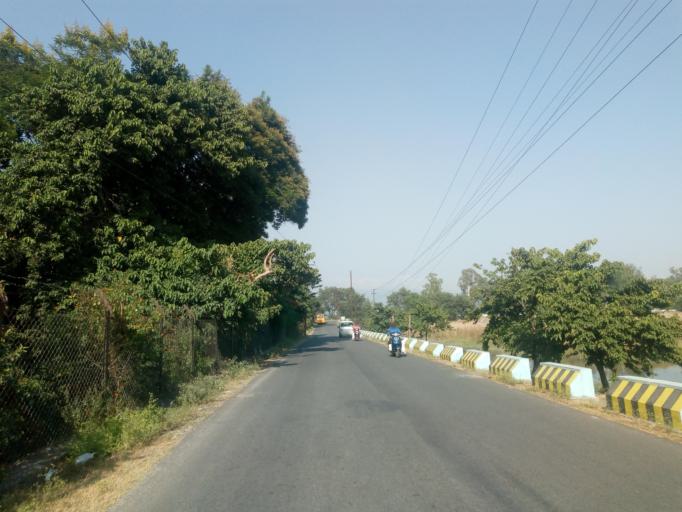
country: IN
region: Himachal Pradesh
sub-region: Sirmaur
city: Paonta Sahib
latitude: 30.4408
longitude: 77.6728
